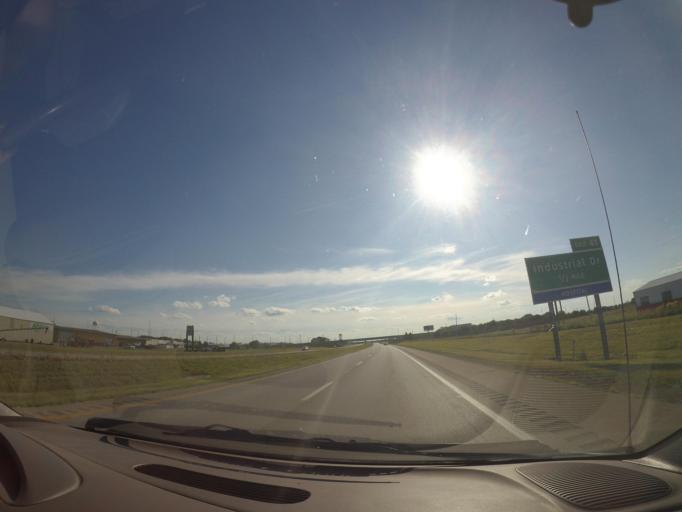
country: US
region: Ohio
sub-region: Henry County
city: Napoleon
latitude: 41.4166
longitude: -84.0919
